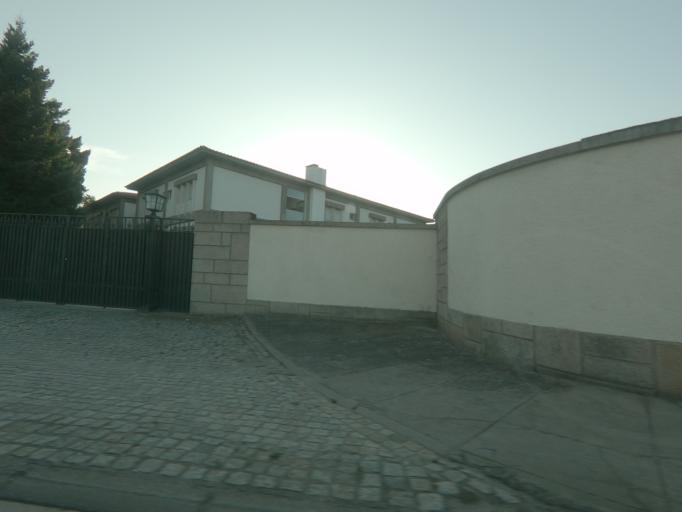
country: PT
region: Vila Real
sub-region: Vila Real
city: Vila Real
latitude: 41.3117
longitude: -7.7346
